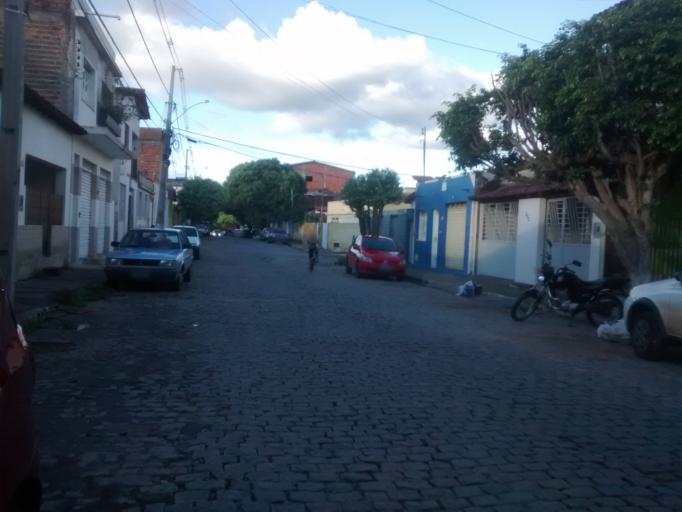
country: BR
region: Bahia
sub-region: Brumado
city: Brumado
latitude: -14.2062
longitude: -41.6725
